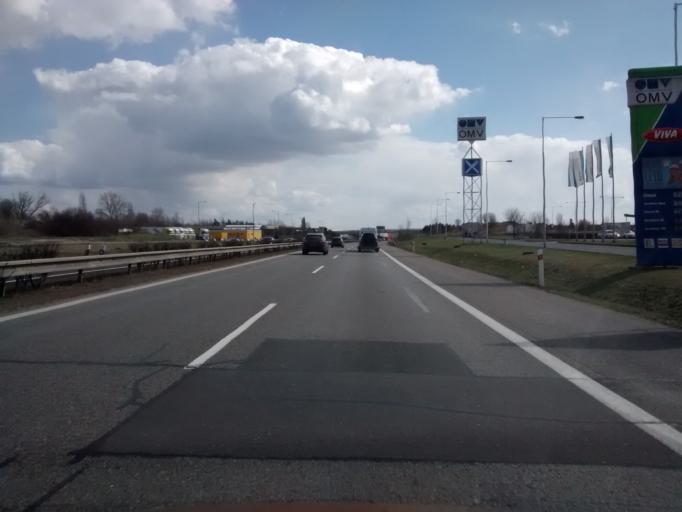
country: CZ
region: Central Bohemia
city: Odolena Voda
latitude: 50.2086
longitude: 14.4335
